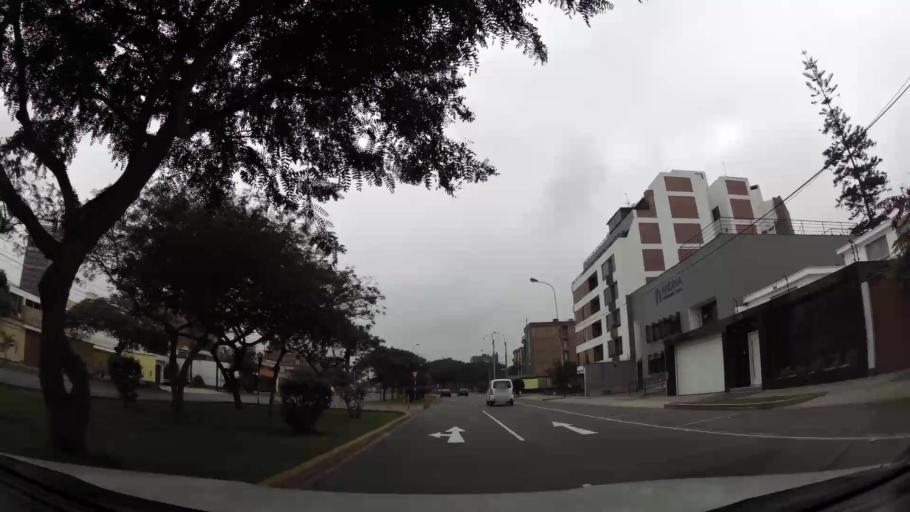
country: PE
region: Lima
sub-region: Lima
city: San Luis
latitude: -12.1007
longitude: -77.0135
